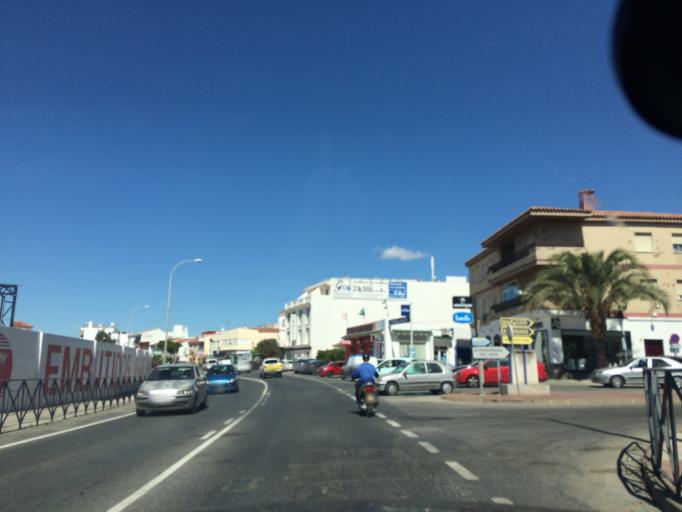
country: ES
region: Andalusia
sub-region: Provincia de Malaga
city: Estacion de Cartama
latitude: 36.7369
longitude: -4.6075
